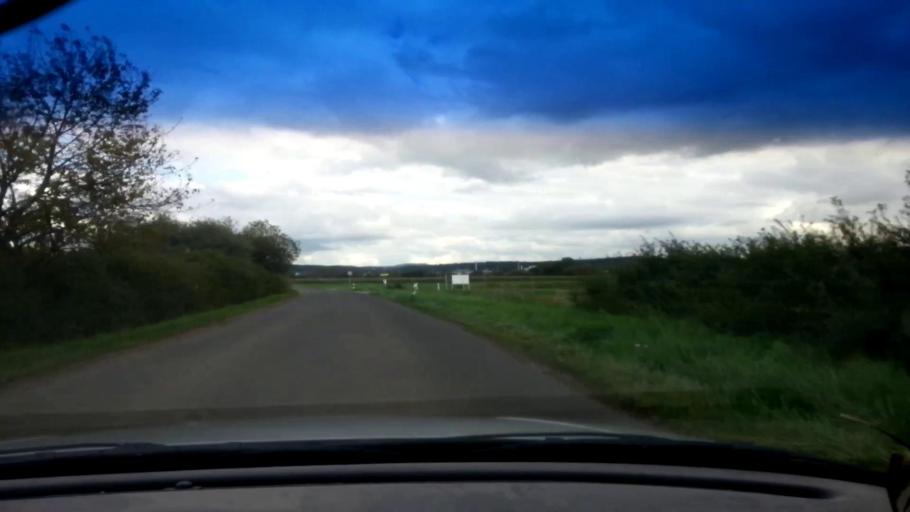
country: DE
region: Bavaria
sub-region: Upper Franconia
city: Rattelsdorf
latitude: 50.0239
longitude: 10.9098
